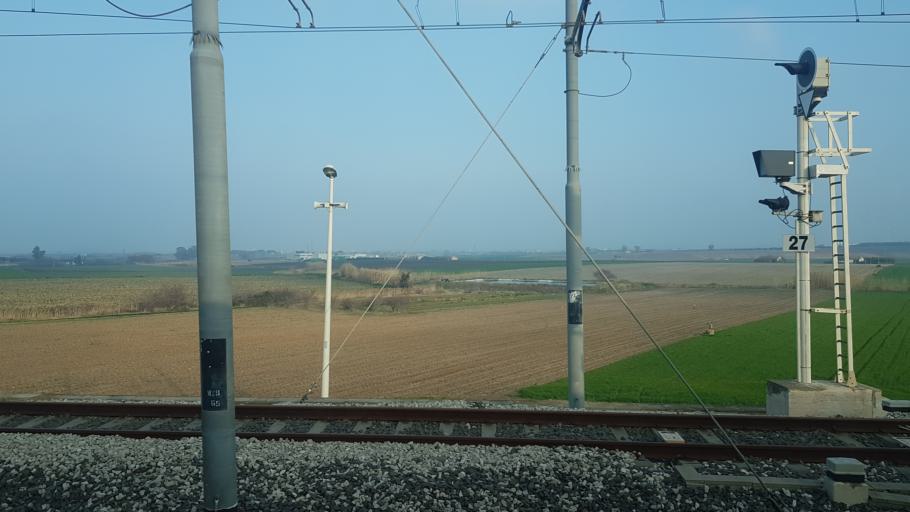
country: IT
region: Apulia
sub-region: Provincia di Foggia
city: Lesina
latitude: 41.8514
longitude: 15.2959
